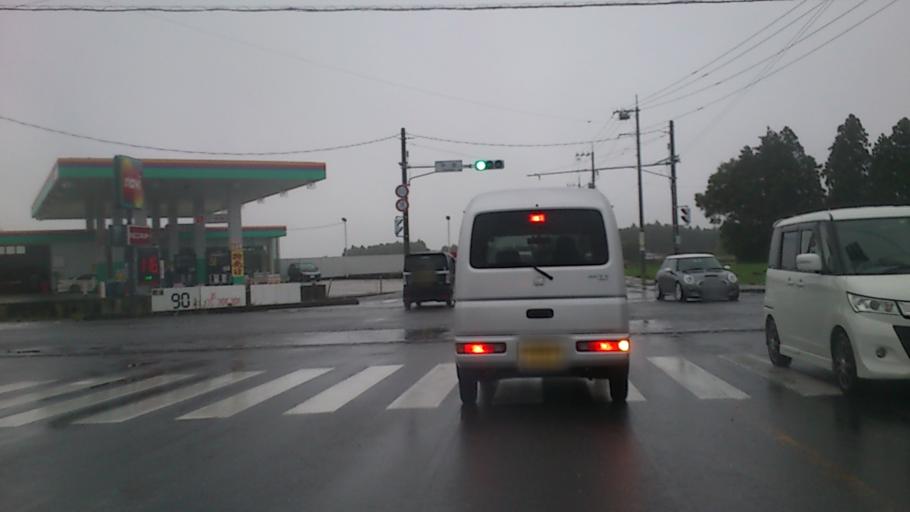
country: JP
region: Tochigi
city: Otawara
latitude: 36.8975
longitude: 140.0182
